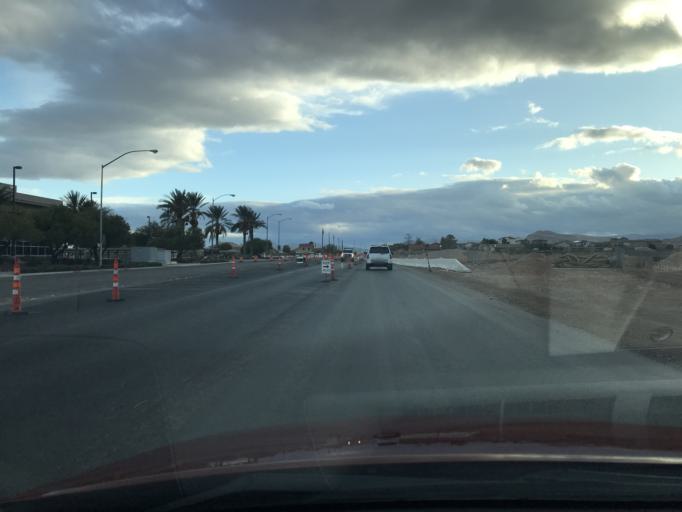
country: US
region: Nevada
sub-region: Clark County
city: Enterprise
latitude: 36.0367
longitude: -115.2791
